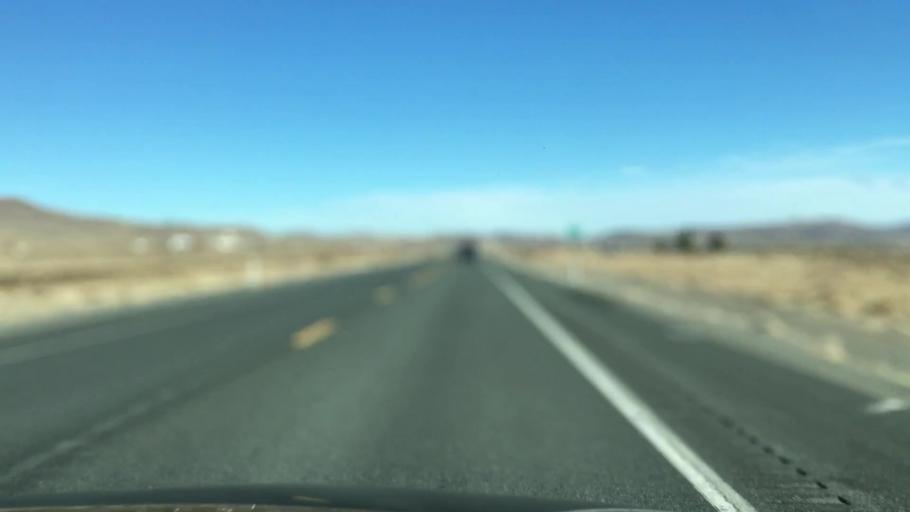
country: US
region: Nevada
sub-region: Lyon County
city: Silver Springs
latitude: 39.4068
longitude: -119.2505
